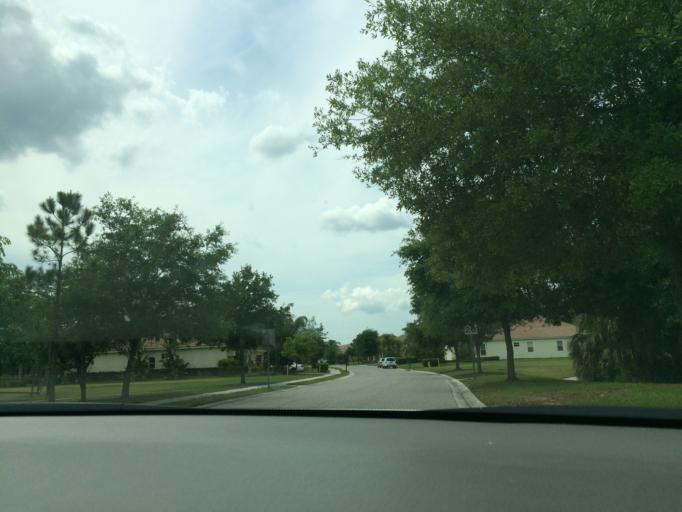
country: US
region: Florida
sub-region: Manatee County
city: Ellenton
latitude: 27.5090
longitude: -82.4167
